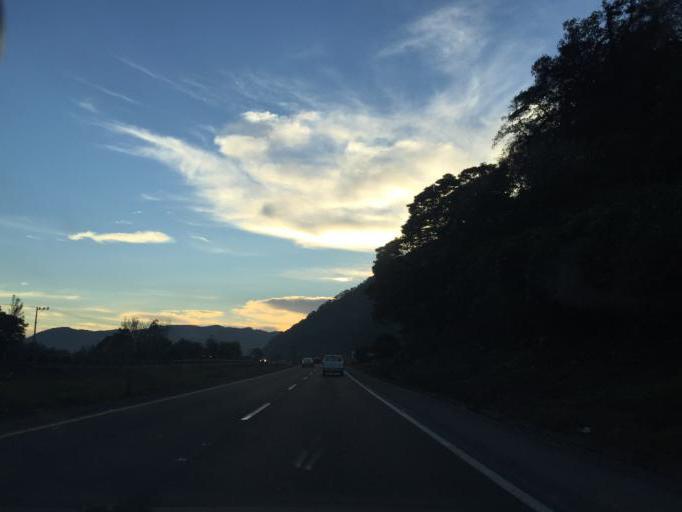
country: MX
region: Veracruz
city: Rio Blanco
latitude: 18.8307
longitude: -97.1263
